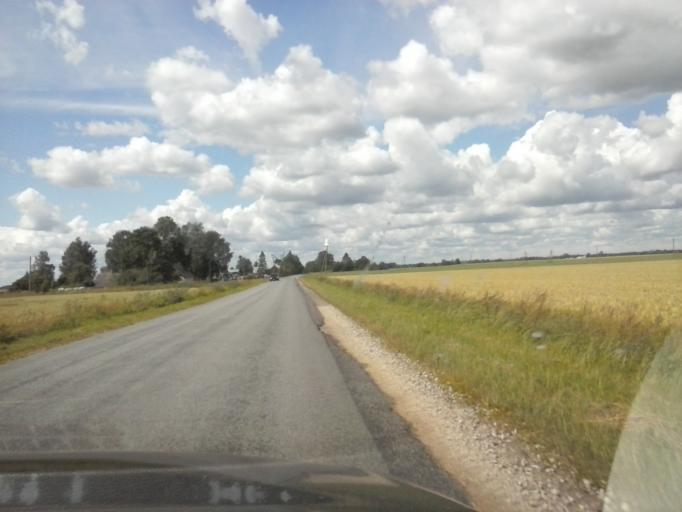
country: EE
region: Laeaene-Virumaa
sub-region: Rakke vald
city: Rakke
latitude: 59.0556
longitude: 26.3467
